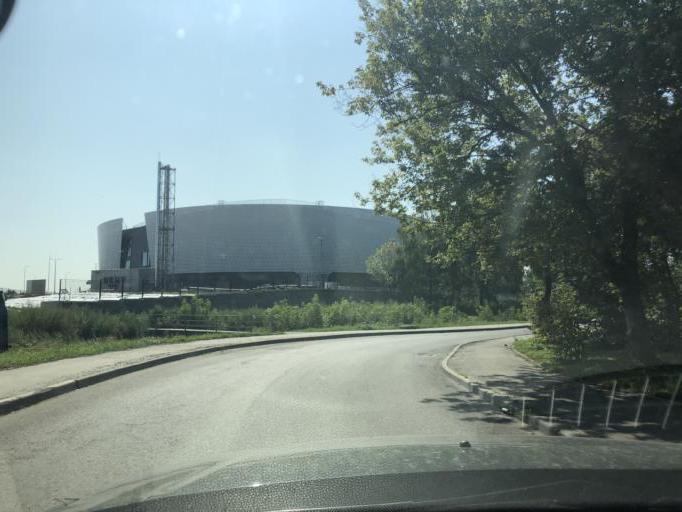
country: RU
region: Tula
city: Tula
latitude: 54.1800
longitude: 37.6414
